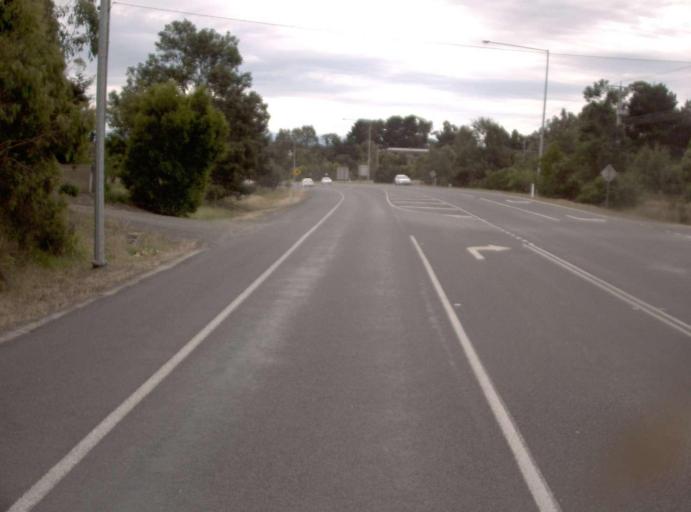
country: AU
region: Victoria
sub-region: Wellington
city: Sale
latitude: -38.1619
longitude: 147.0860
